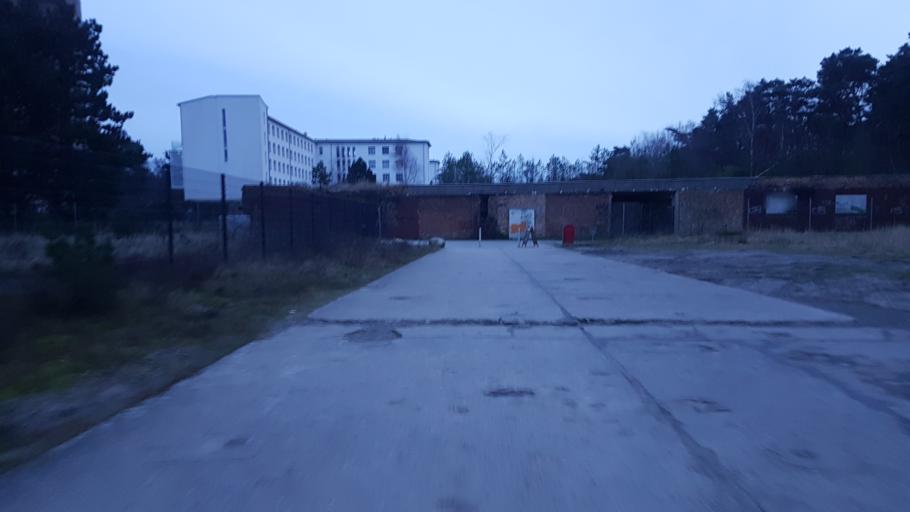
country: DE
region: Mecklenburg-Vorpommern
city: Ostseebad Binz
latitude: 54.4479
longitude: 13.5705
